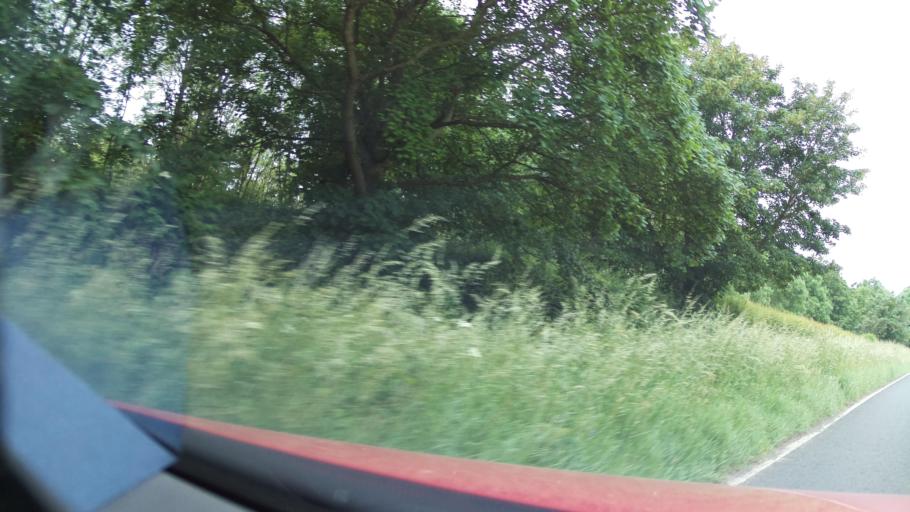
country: GB
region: England
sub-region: District of Rutland
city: Empingham
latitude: 52.6666
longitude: -0.6085
